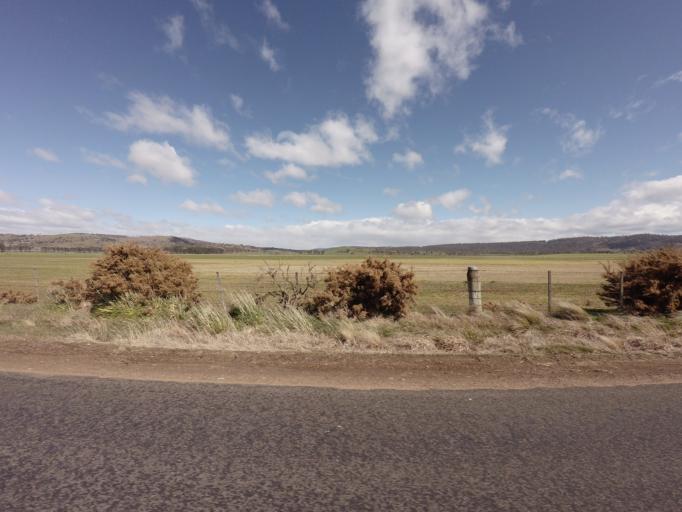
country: AU
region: Tasmania
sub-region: Northern Midlands
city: Evandale
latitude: -42.0199
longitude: 147.4686
